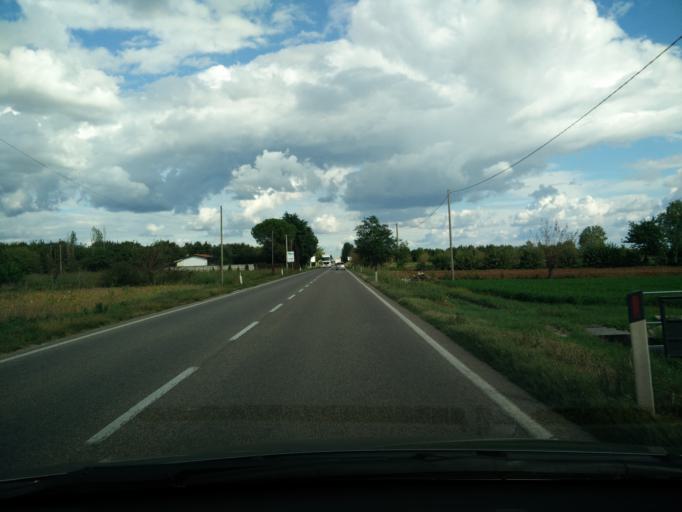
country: IT
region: Veneto
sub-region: Provincia di Treviso
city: Fossalunga
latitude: 45.7038
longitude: 12.0363
